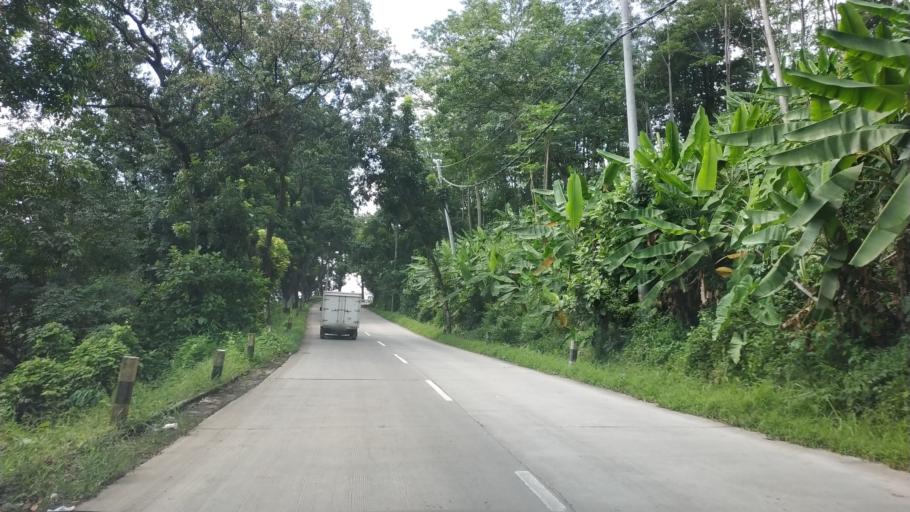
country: ID
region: Central Java
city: Weleri
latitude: -7.0002
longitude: 110.0627
